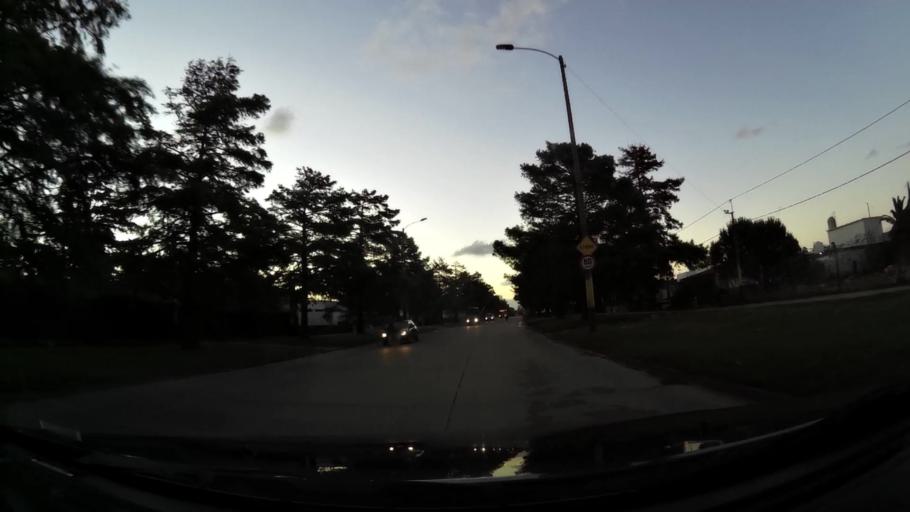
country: UY
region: Canelones
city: Paso de Carrasco
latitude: -34.8716
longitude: -56.1029
